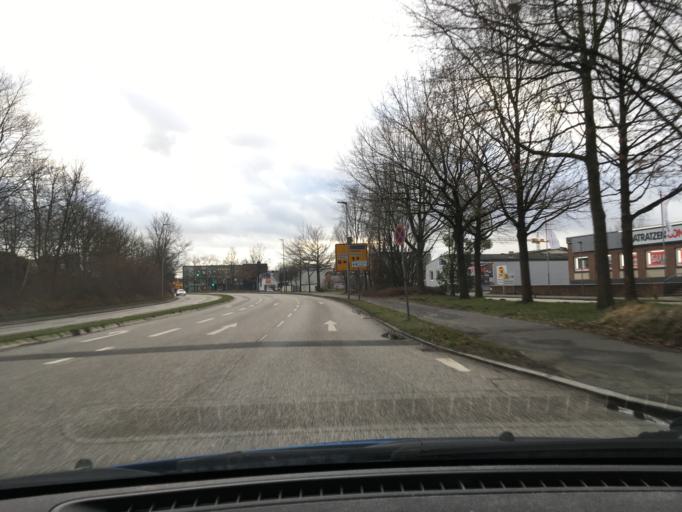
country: DE
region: Schleswig-Holstein
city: Itzehoe
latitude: 53.9205
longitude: 9.5130
